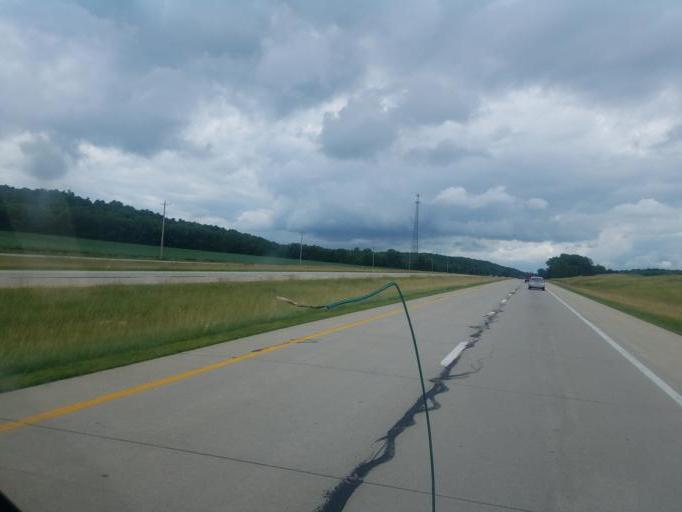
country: US
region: Ohio
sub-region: Logan County
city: Bellefontaine
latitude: 40.3254
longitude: -83.6404
